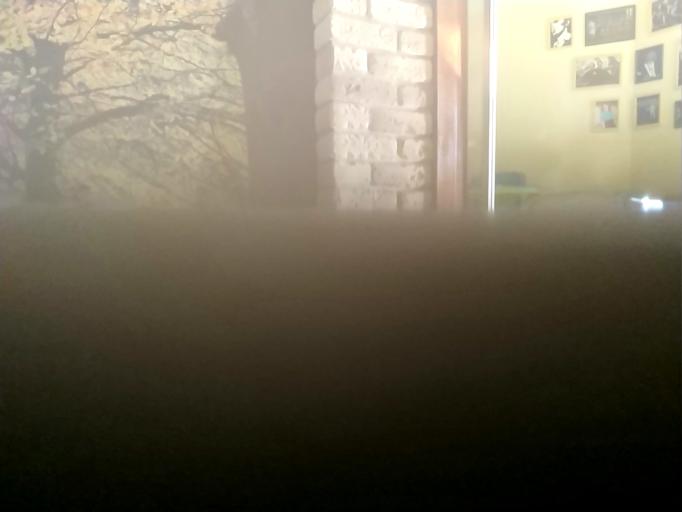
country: RU
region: Smolensk
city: Temkino
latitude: 54.8722
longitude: 34.9862
